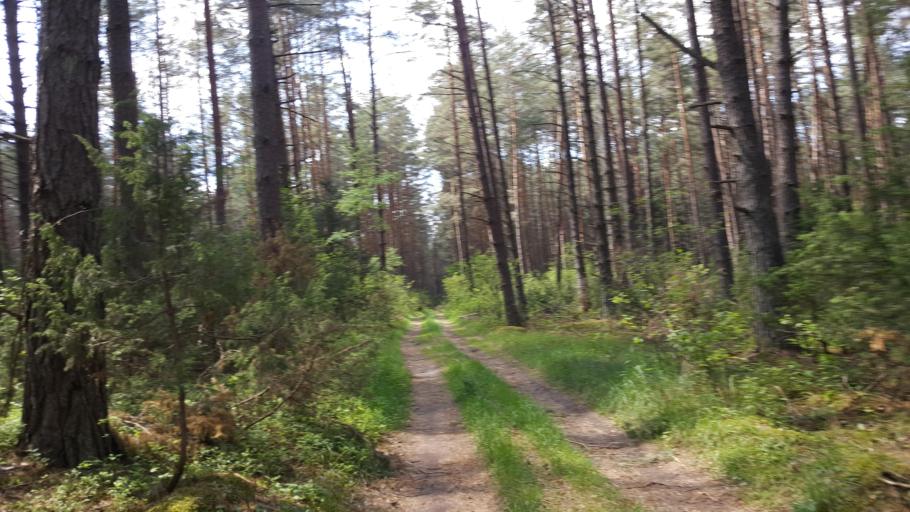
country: BY
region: Brest
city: Kamyanyets
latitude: 52.4485
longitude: 24.0041
